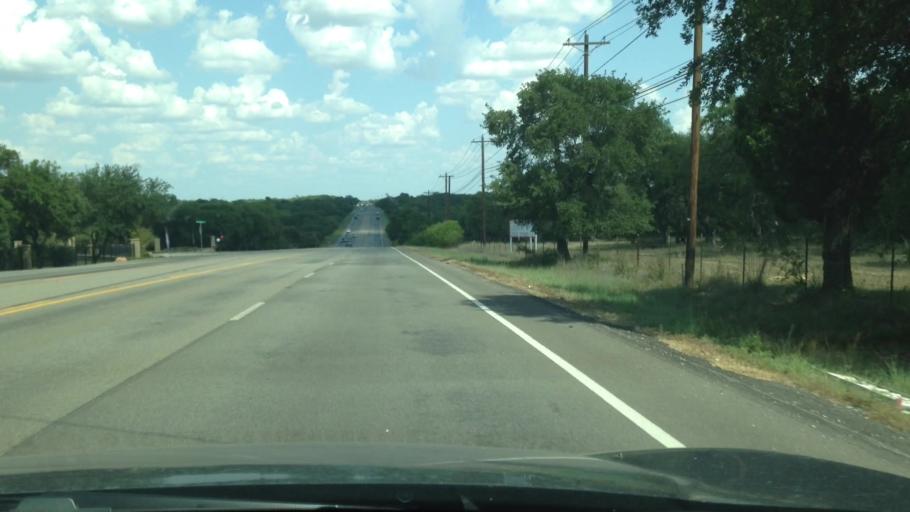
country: US
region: Texas
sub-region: Williamson County
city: Georgetown
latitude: 30.6337
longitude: -97.7732
